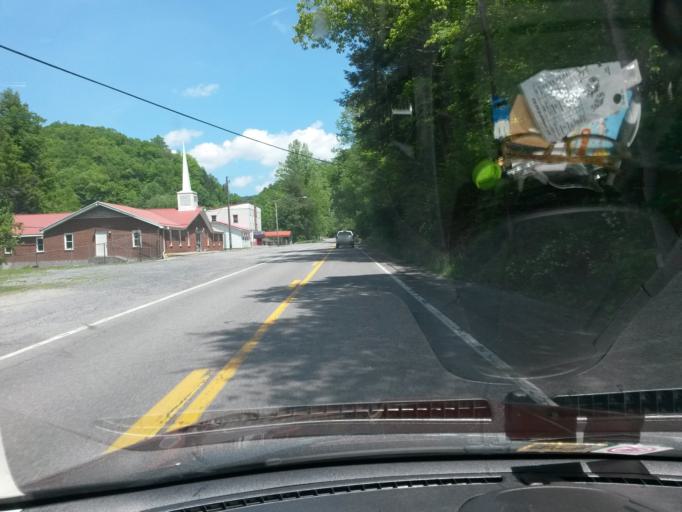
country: US
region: West Virginia
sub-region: McDowell County
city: Welch
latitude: 37.4701
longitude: -81.5416
